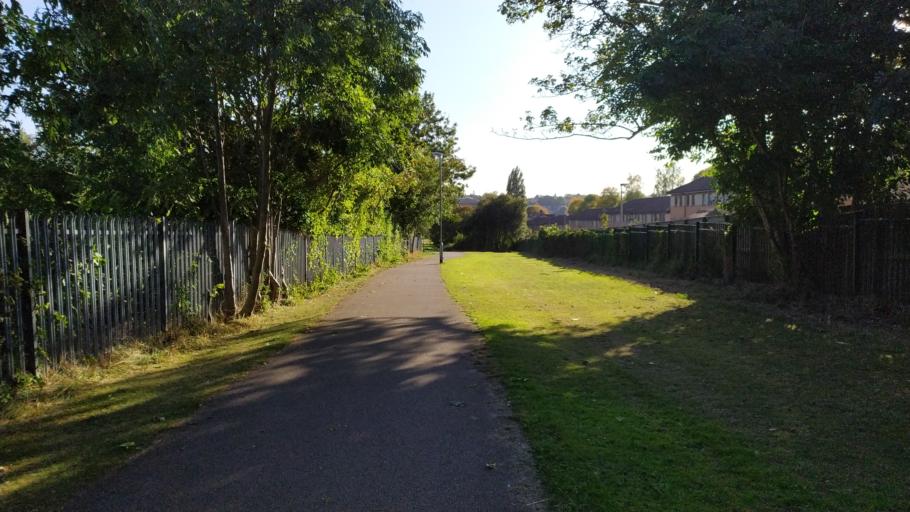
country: GB
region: England
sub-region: City and Borough of Leeds
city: Chapel Allerton
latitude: 53.8291
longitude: -1.5580
